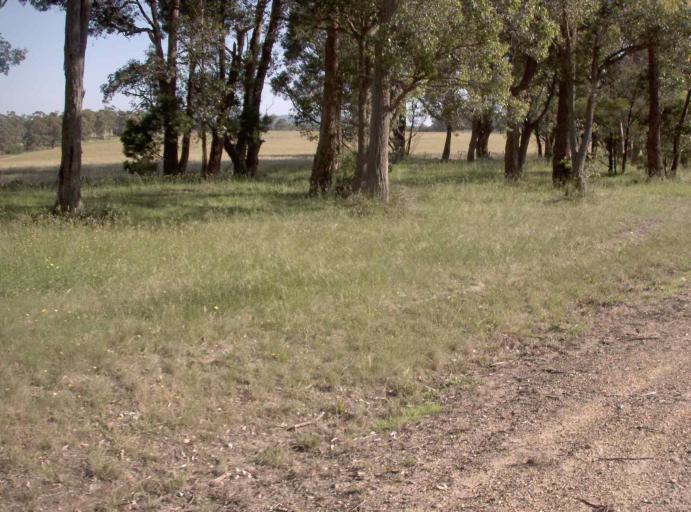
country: AU
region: Victoria
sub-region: East Gippsland
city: Lakes Entrance
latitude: -37.6972
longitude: 148.4646
